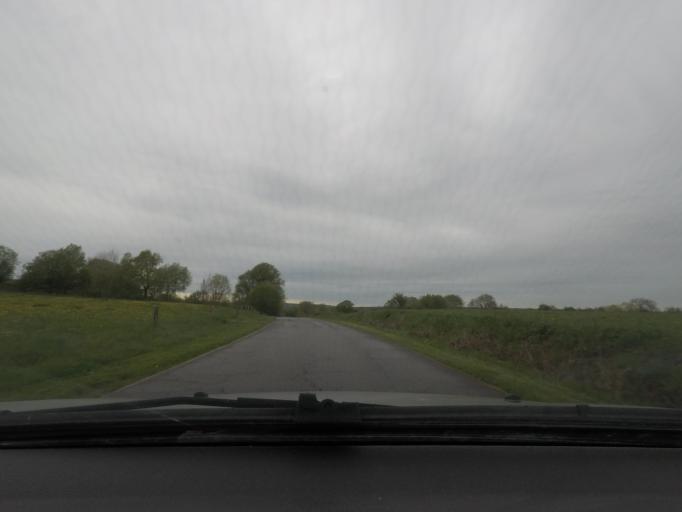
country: BE
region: Wallonia
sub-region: Province du Luxembourg
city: Etalle
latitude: 49.7088
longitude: 5.5665
